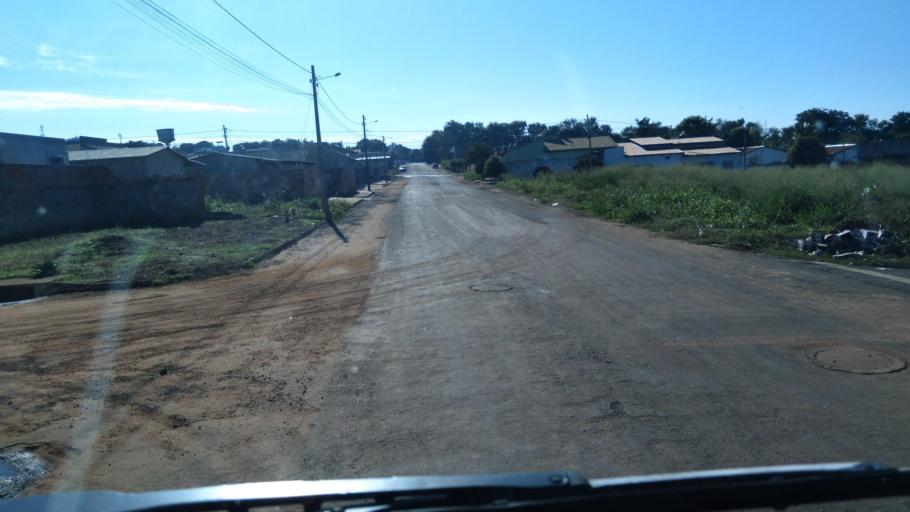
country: BR
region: Goias
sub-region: Mineiros
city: Mineiros
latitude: -17.5763
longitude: -52.5696
